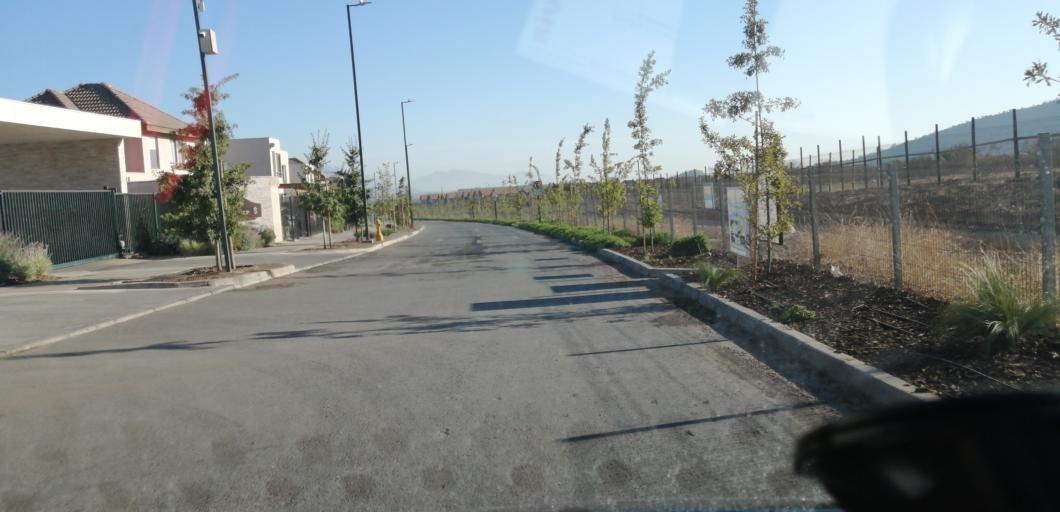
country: CL
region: Santiago Metropolitan
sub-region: Provincia de Santiago
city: Lo Prado
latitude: -33.4693
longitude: -70.8596
